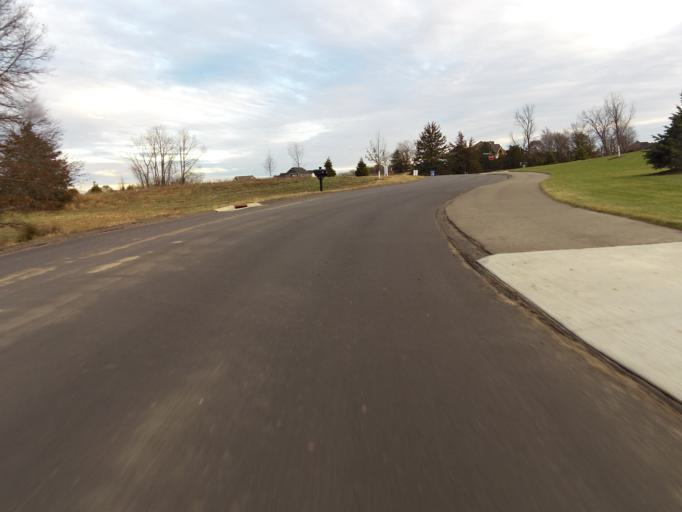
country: US
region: Minnesota
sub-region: Washington County
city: Bayport
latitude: 45.0026
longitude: -92.7995
